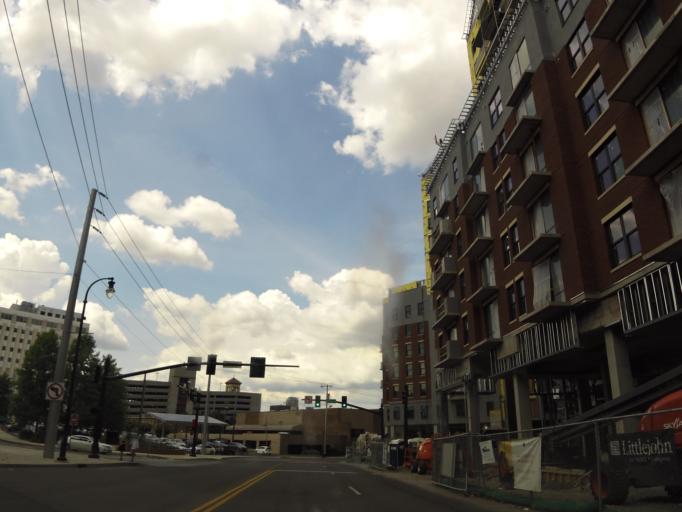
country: US
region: Tennessee
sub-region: Davidson County
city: Nashville
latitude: 36.1478
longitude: -86.7993
